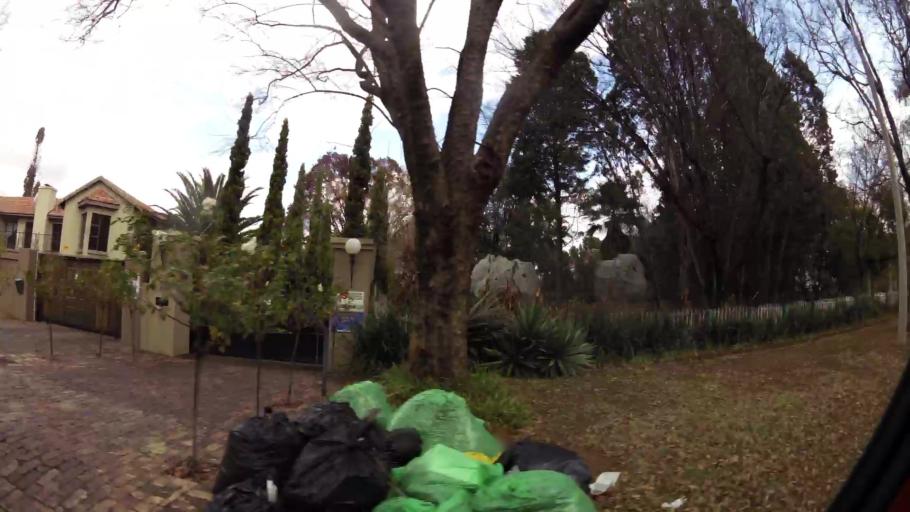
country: ZA
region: Gauteng
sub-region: Sedibeng District Municipality
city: Vanderbijlpark
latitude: -26.7419
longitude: 27.8296
